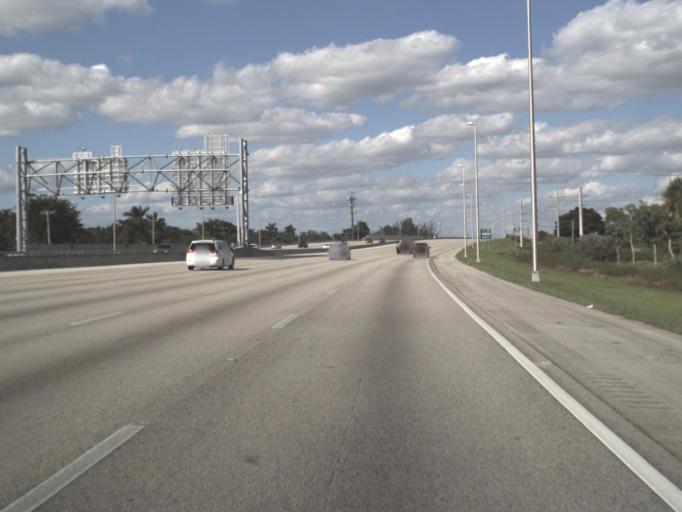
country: US
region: Florida
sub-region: Broward County
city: Broadview Park
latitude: 26.1158
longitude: -80.2184
